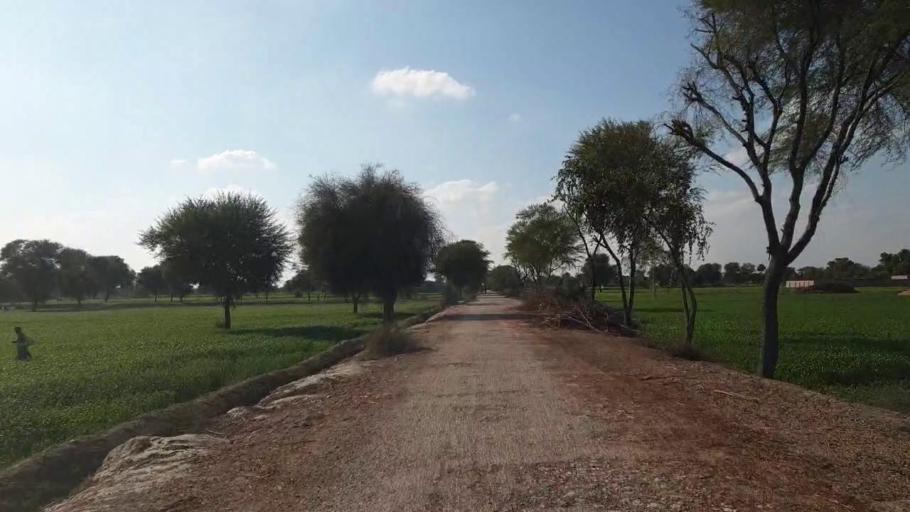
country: PK
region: Sindh
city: Shahpur Chakar
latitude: 26.1095
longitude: 68.5601
